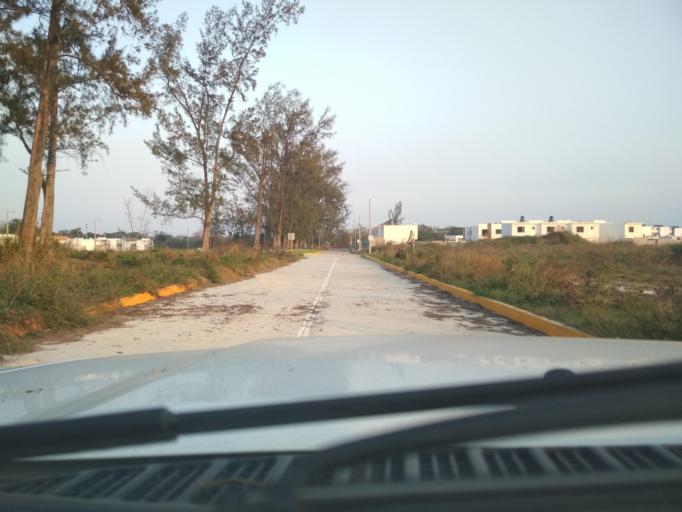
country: MX
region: Veracruz
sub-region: Veracruz
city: Las Amapolas
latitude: 19.1422
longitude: -96.2226
